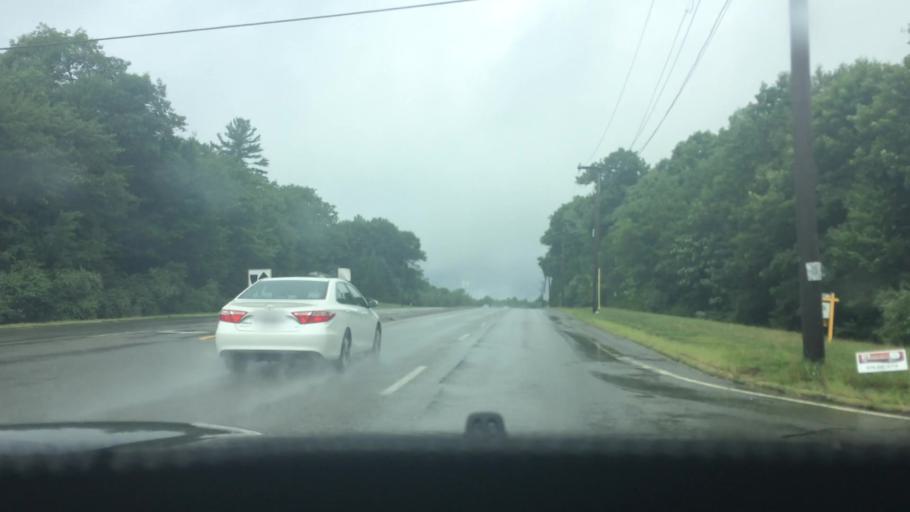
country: US
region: Massachusetts
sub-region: Worcester County
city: Westminster
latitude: 42.5624
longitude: -71.9385
